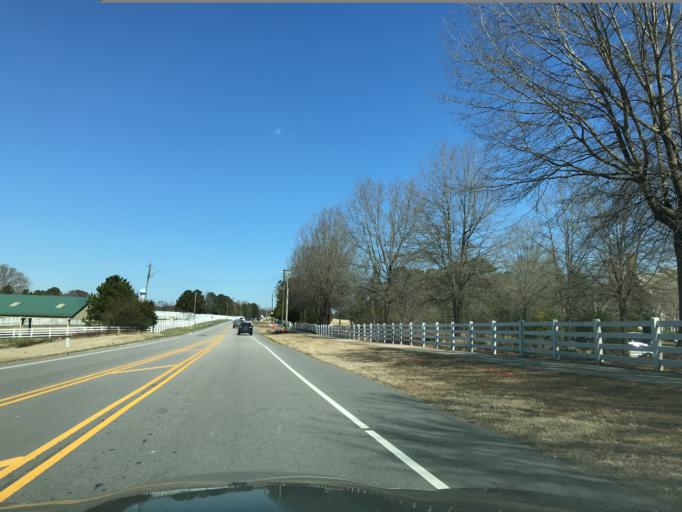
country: US
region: North Carolina
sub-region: Wake County
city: Wake Forest
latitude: 35.9547
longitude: -78.5666
